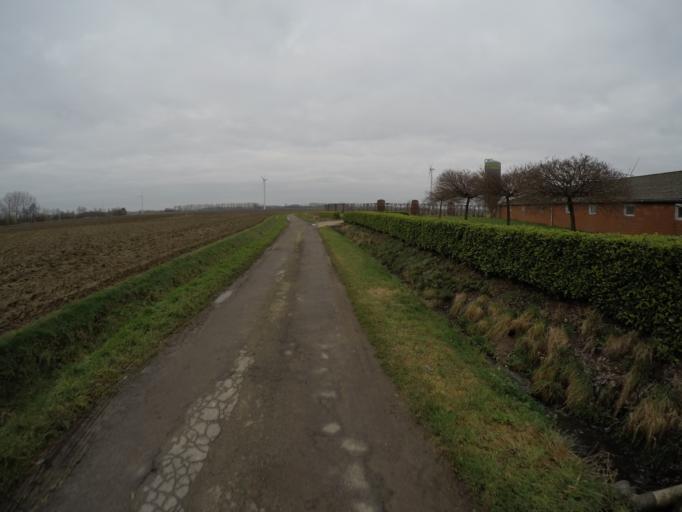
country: BE
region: Flanders
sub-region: Provincie Oost-Vlaanderen
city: Sint-Gillis-Waas
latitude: 51.2293
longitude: 4.1828
